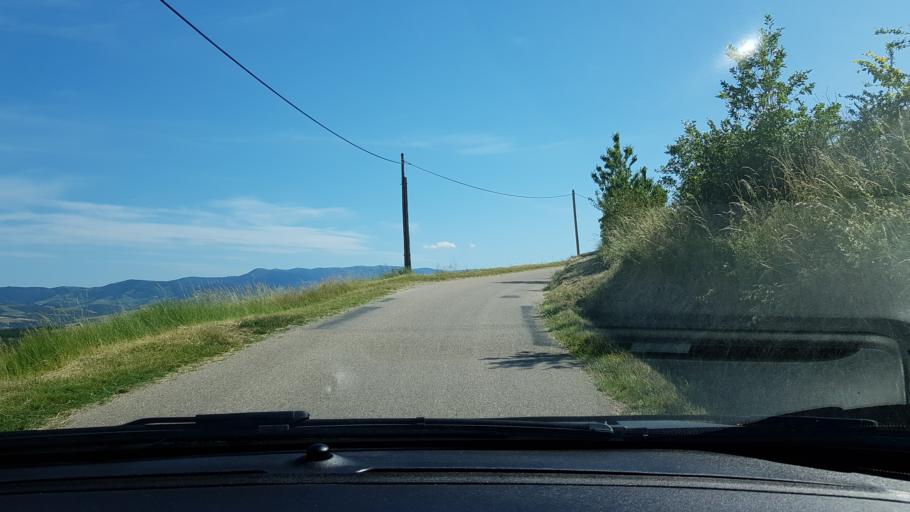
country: FR
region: Rhone-Alpes
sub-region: Departement du Rhone
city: Saint-Didier-sous-Riverie
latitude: 45.5809
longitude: 4.5949
